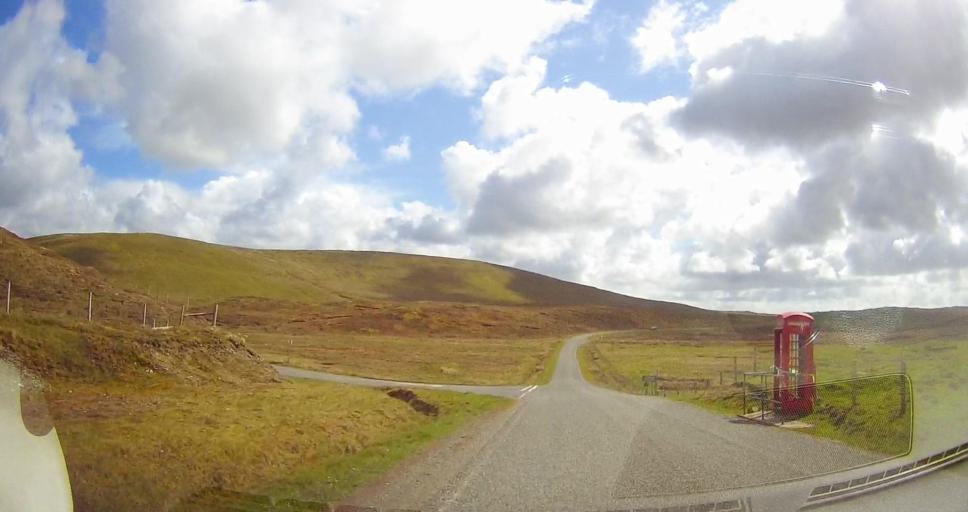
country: GB
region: Scotland
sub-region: Shetland Islands
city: Lerwick
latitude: 60.5188
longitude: -1.3775
